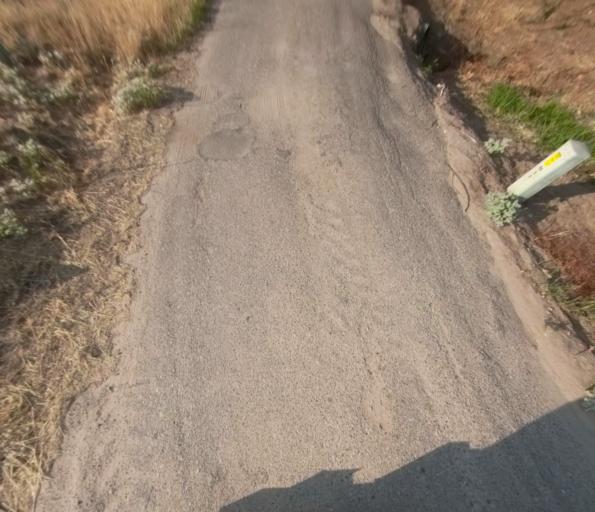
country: US
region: California
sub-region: Madera County
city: Yosemite Lakes
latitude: 37.2128
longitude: -119.9058
